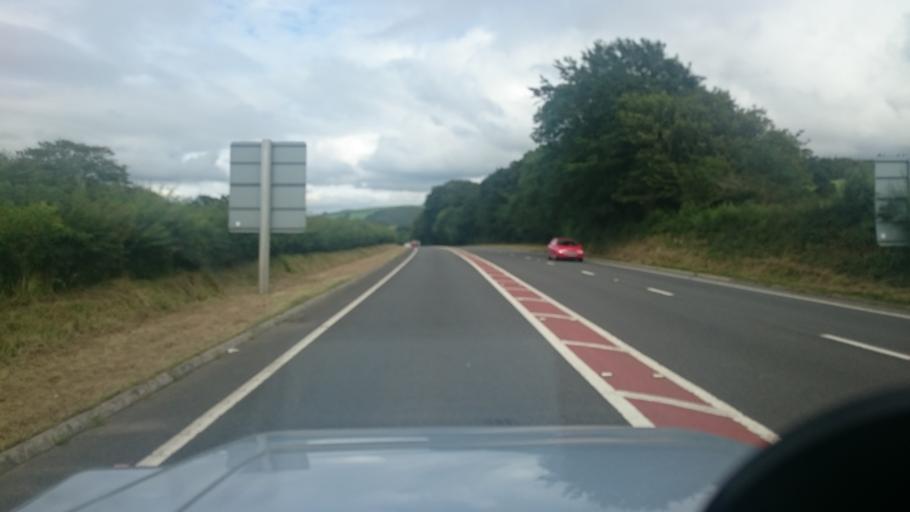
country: GB
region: Wales
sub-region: Pembrokeshire
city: Wiston
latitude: 51.8011
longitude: -4.8193
